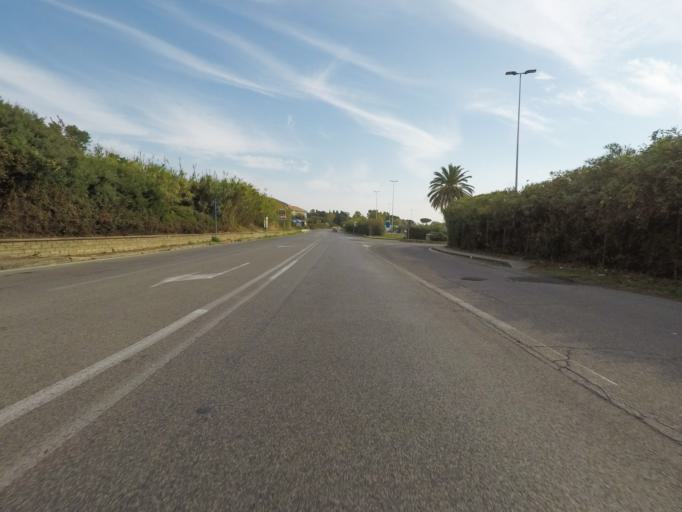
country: IT
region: Latium
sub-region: Citta metropolitana di Roma Capitale
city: Civitavecchia
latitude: 42.0621
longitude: 11.8156
